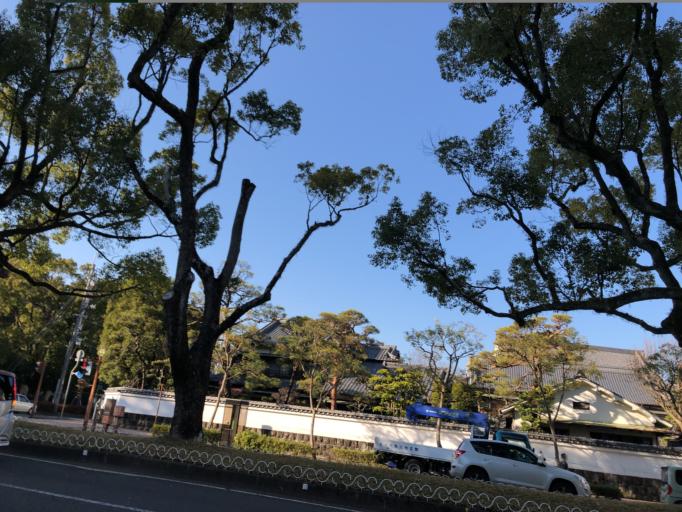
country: JP
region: Kochi
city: Kochi-shi
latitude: 33.5607
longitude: 133.5349
